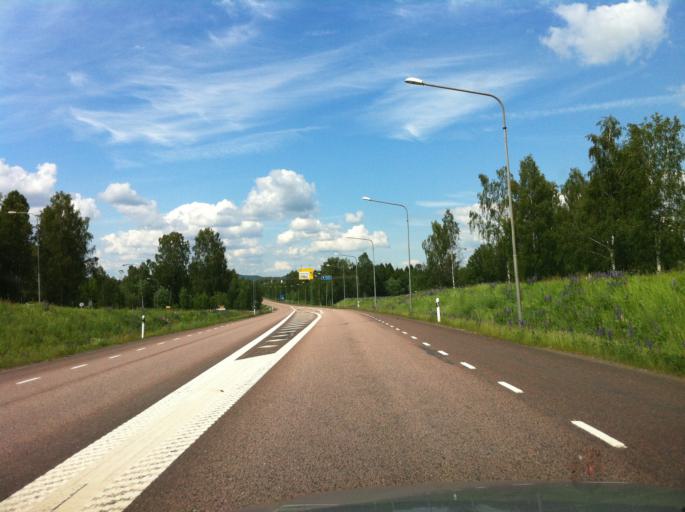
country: SE
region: Vaermland
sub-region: Sunne Kommun
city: Sunne
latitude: 59.8305
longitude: 13.1318
